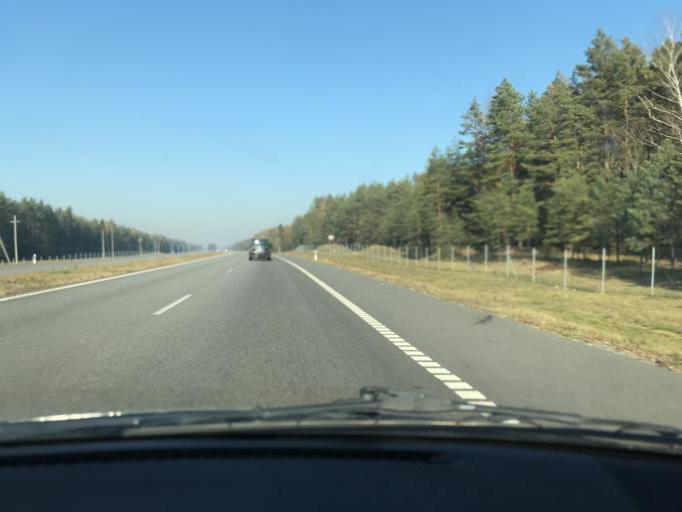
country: BY
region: Minsk
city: Slutsk
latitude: 53.2866
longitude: 27.5497
